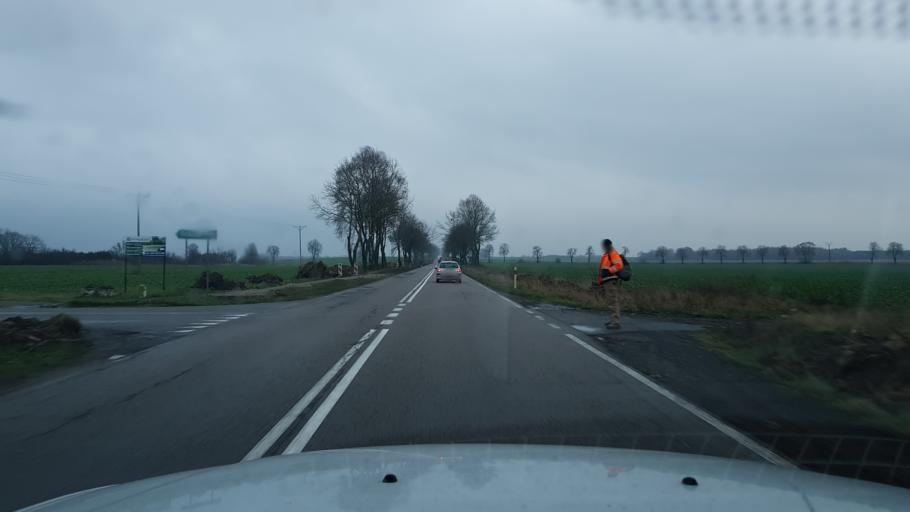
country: PL
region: West Pomeranian Voivodeship
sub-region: Powiat gryficki
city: Ploty
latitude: 53.8455
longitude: 15.2330
